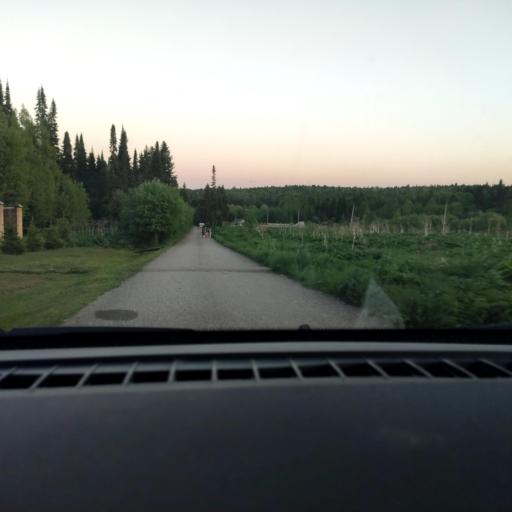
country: RU
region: Perm
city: Ferma
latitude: 57.9862
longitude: 56.3779
